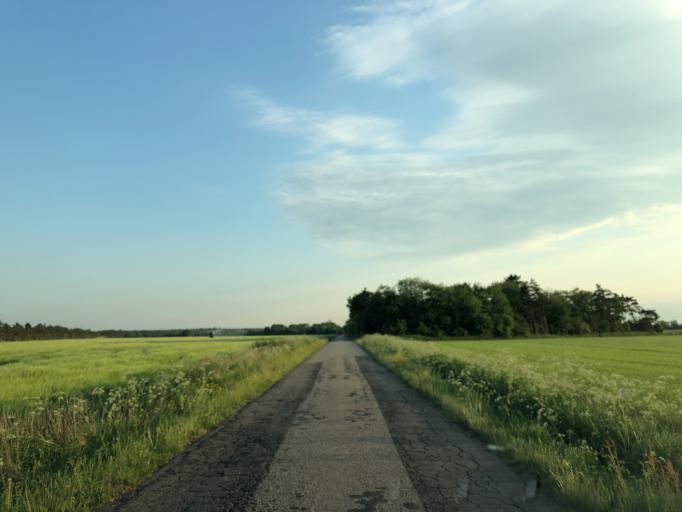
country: DK
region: Central Jutland
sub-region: Holstebro Kommune
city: Holstebro
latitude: 56.3813
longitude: 8.4641
